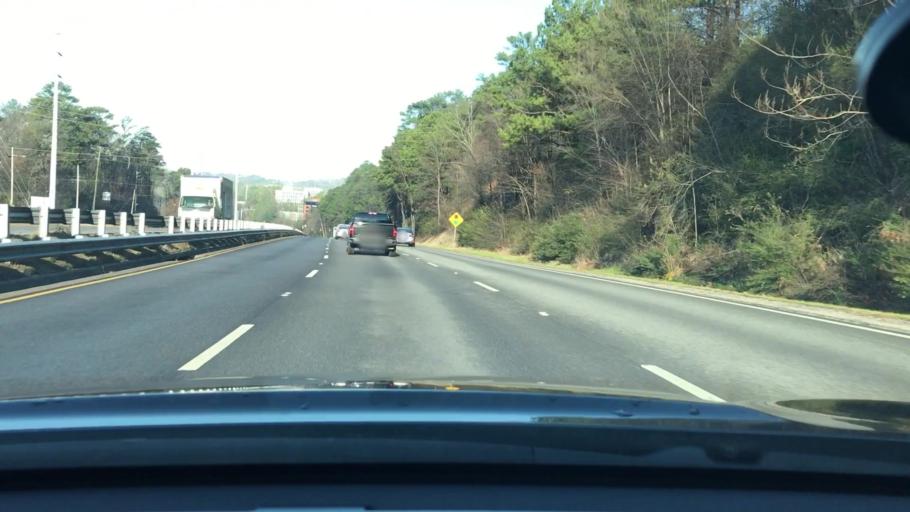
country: US
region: Alabama
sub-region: Jefferson County
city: Cahaba Heights
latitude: 33.4692
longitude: -86.7586
